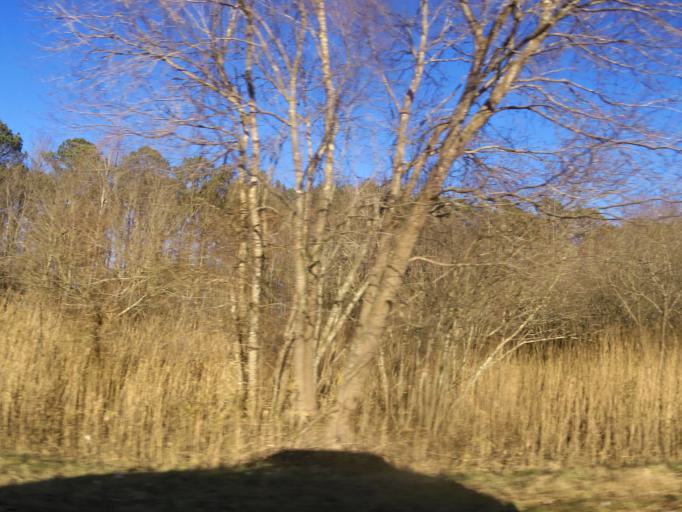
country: US
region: Virginia
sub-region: City of Franklin
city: Franklin
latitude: 36.6671
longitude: -76.8868
